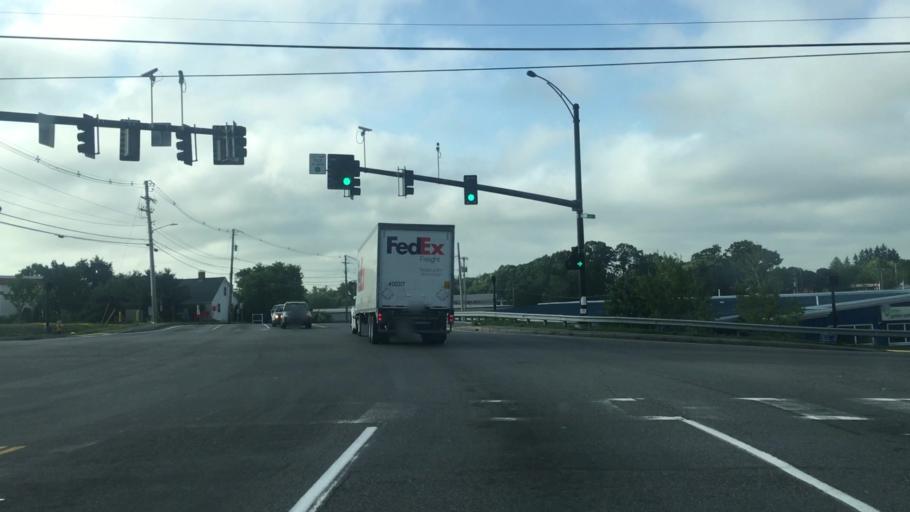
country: US
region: Maine
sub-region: Cumberland County
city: Westbrook
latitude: 43.6859
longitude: -70.3281
